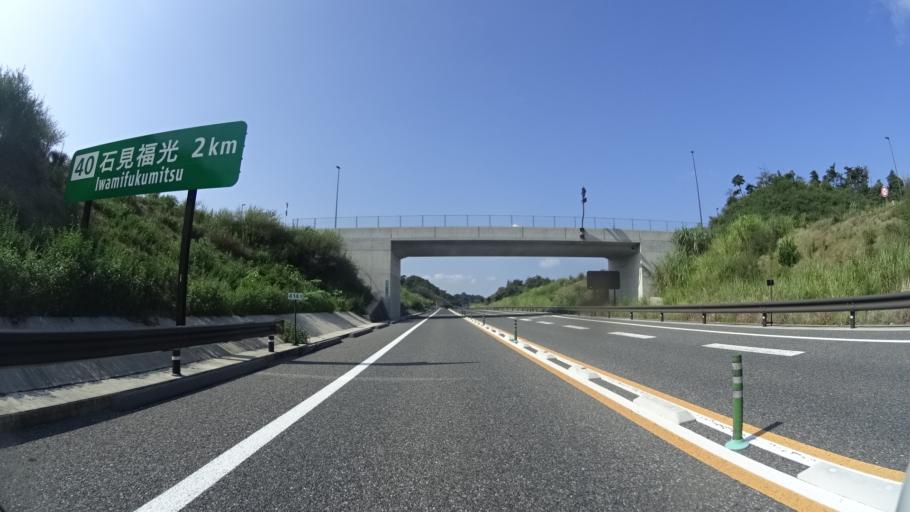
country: JP
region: Shimane
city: Gotsucho
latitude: 35.0827
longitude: 132.3447
